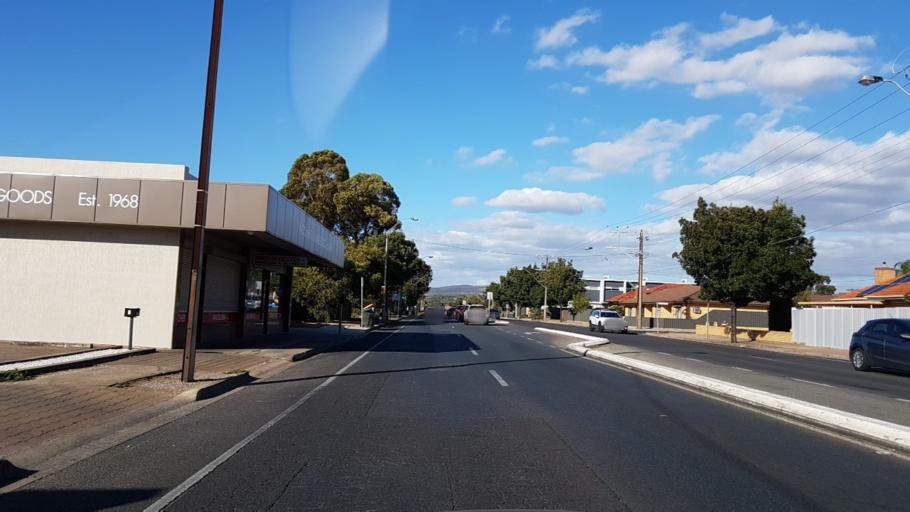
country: AU
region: South Australia
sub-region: Campbelltown
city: Paradise
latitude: -34.8756
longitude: 138.6667
